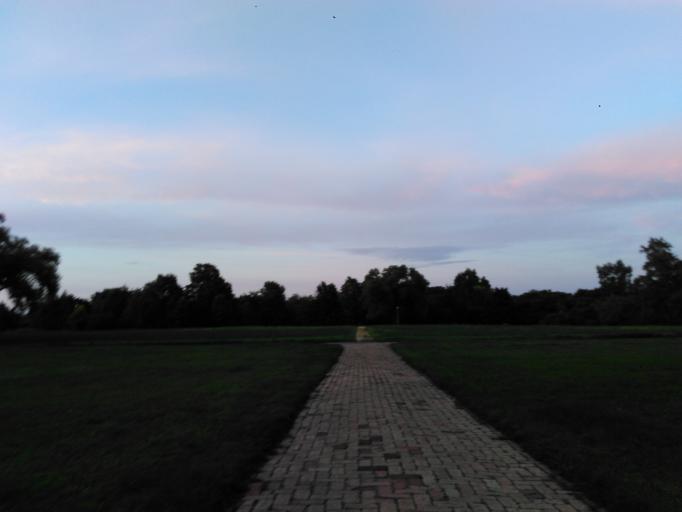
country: RU
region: Penza
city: Lermontovo
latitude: 52.9929
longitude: 43.6740
